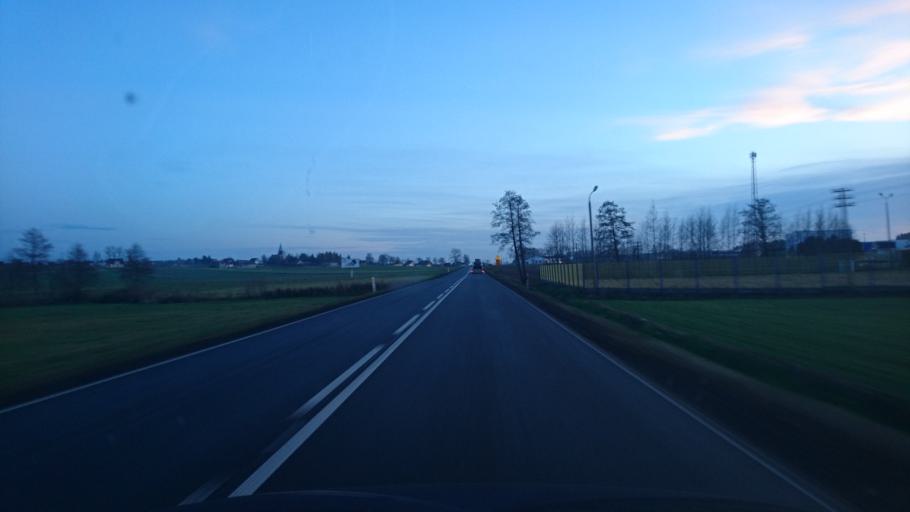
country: PL
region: Greater Poland Voivodeship
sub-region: Powiat ostrzeszowski
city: Ostrzeszow
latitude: 51.3927
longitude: 17.9441
